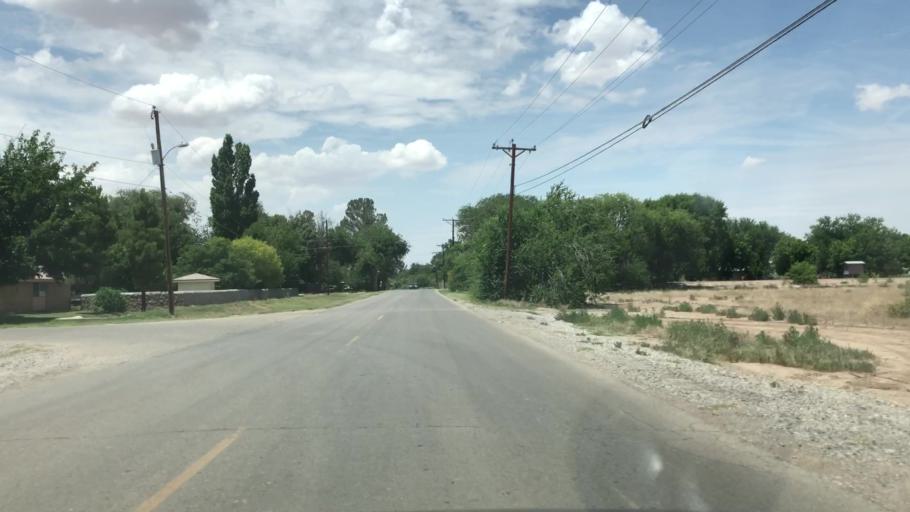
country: US
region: Texas
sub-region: El Paso County
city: Canutillo
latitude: 31.9090
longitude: -106.6322
